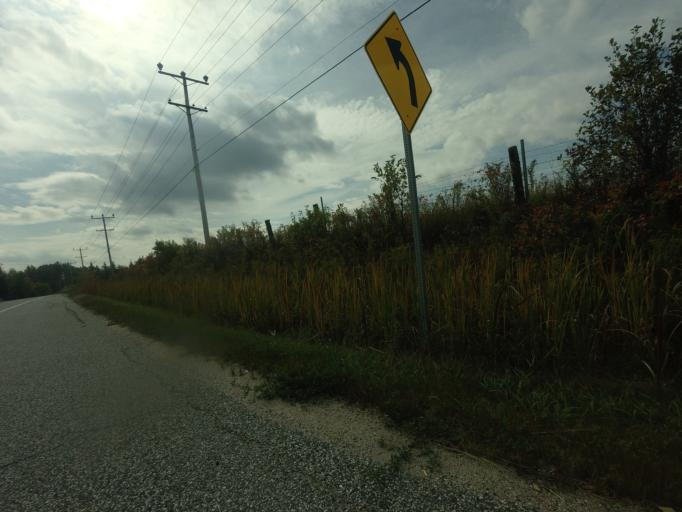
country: CA
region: Quebec
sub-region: Outaouais
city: Wakefield
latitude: 45.8524
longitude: -75.9970
